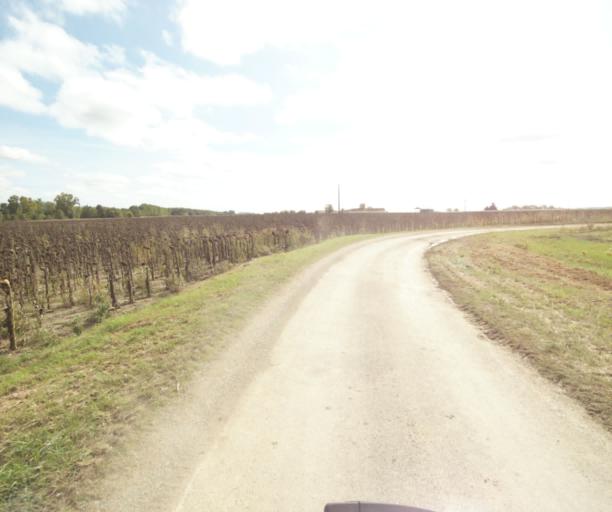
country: FR
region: Midi-Pyrenees
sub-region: Departement du Tarn-et-Garonne
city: Montech
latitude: 43.9454
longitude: 1.2067
